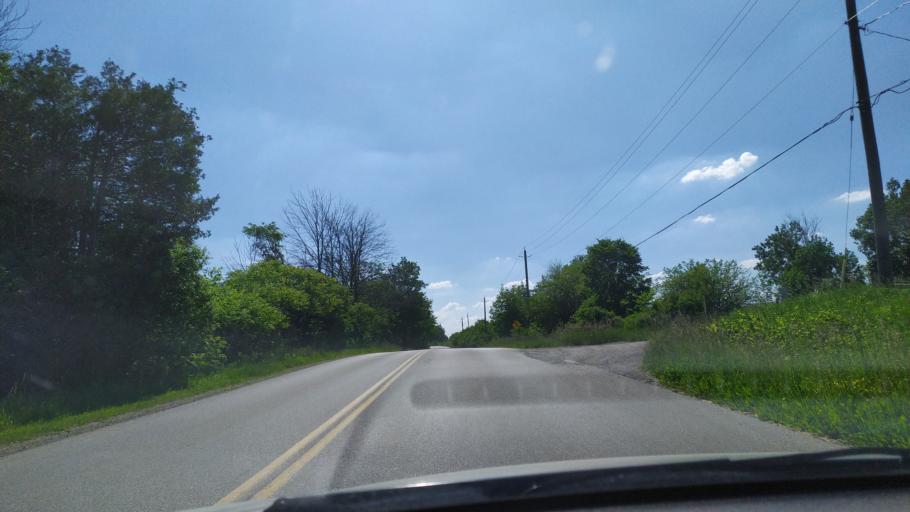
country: CA
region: Ontario
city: Kitchener
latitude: 43.3710
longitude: -80.5618
